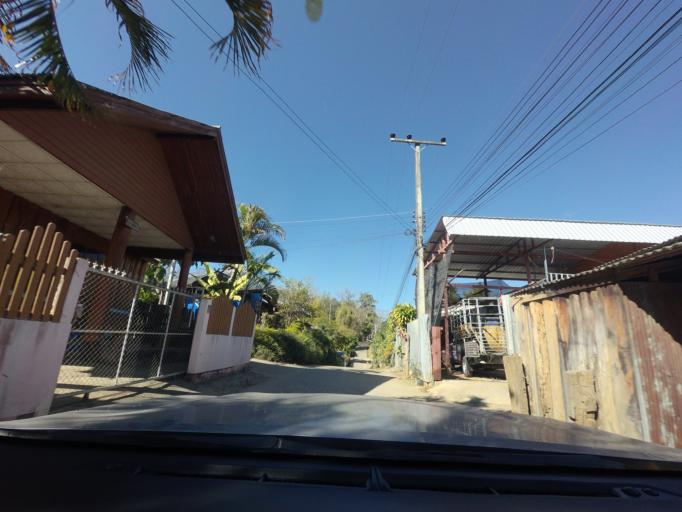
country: TH
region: Mae Hong Son
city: Wiang Nuea
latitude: 19.3964
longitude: 98.4217
